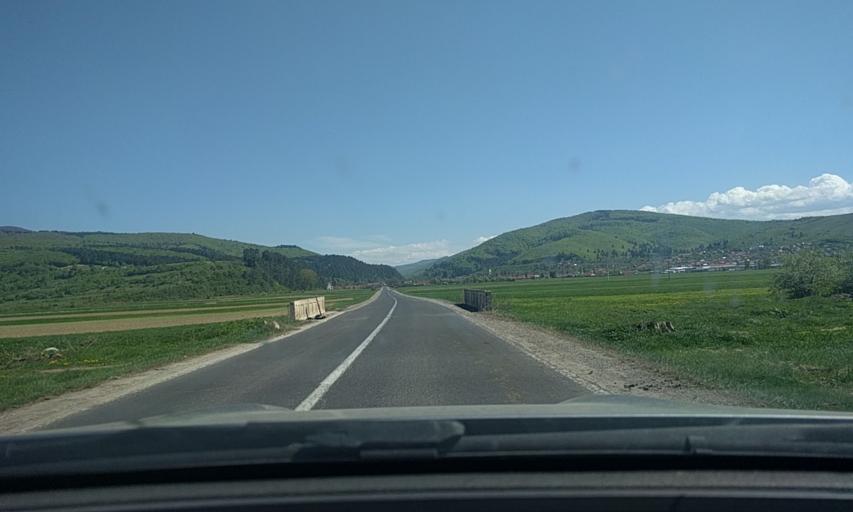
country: RO
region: Brasov
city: Tunelu-Teliu
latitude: 45.7081
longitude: 25.8333
